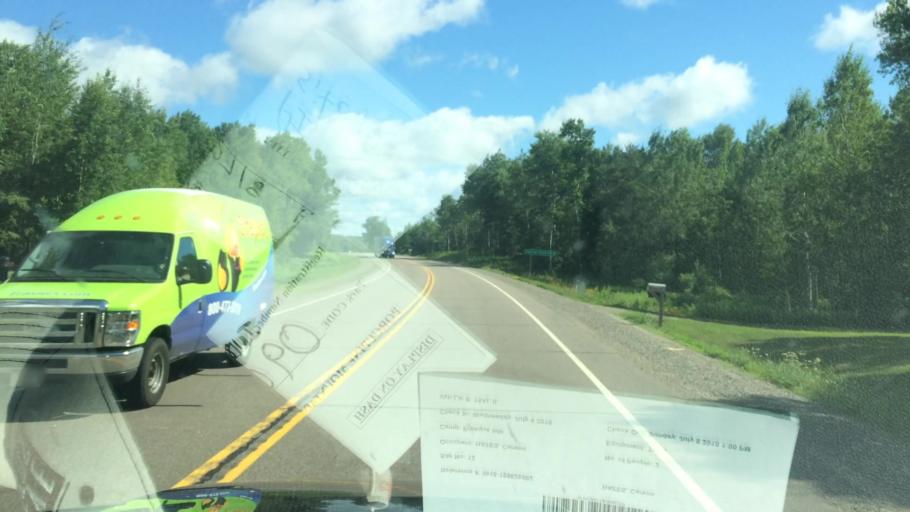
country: US
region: Wisconsin
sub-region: Oneida County
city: Rhinelander
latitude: 45.5737
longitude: -89.5712
